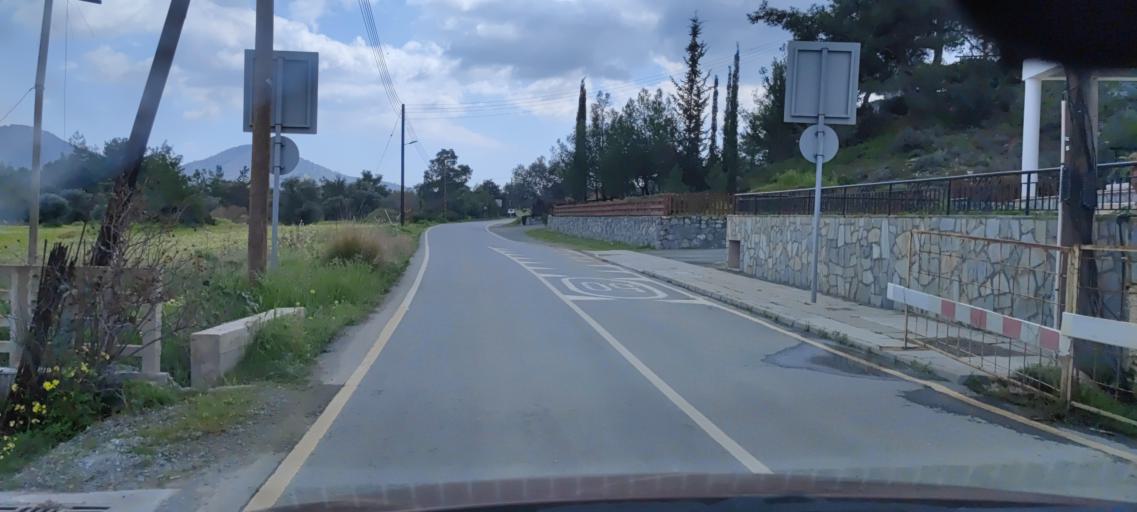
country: CY
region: Larnaka
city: Kornos
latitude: 34.9143
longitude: 33.4024
